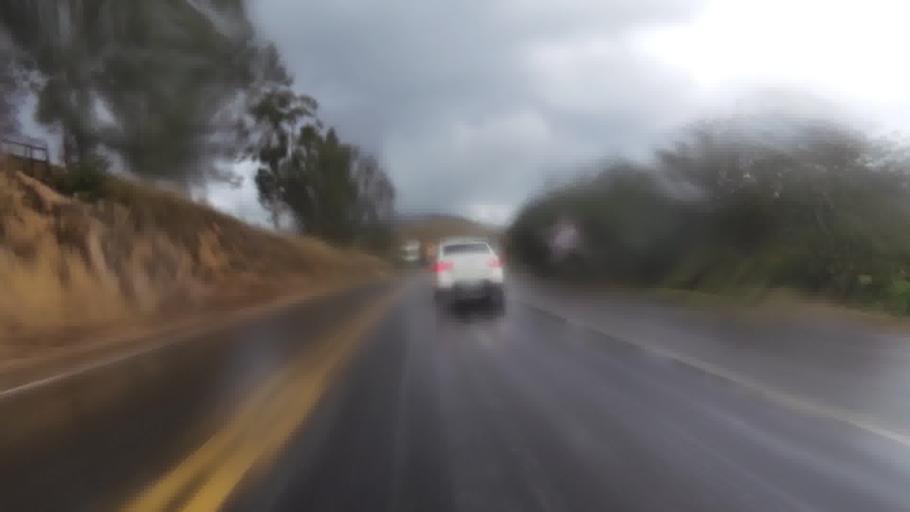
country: BR
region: Espirito Santo
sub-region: Cachoeiro De Itapemirim
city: Cachoeiro de Itapemirim
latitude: -20.9587
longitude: -41.0996
